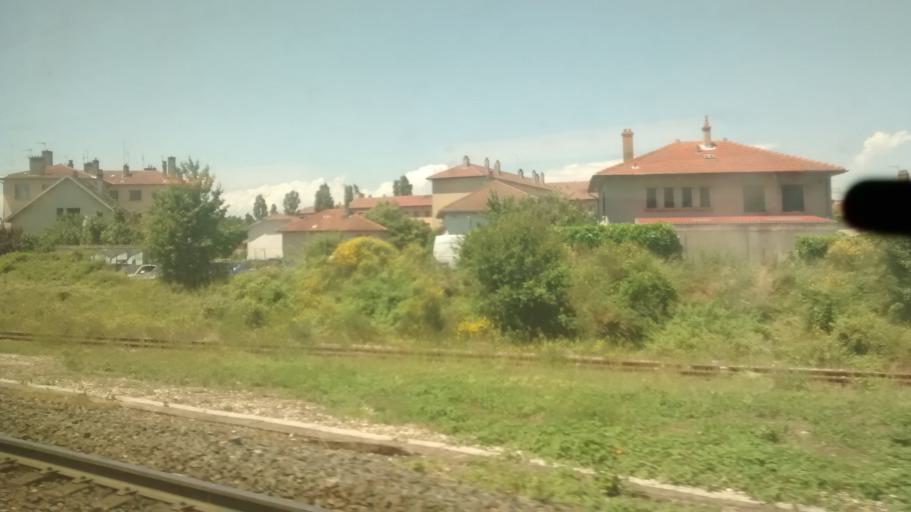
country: FR
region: Rhone-Alpes
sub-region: Departement du Rhone
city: Sathonay-Camp
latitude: 45.8215
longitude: 4.8780
